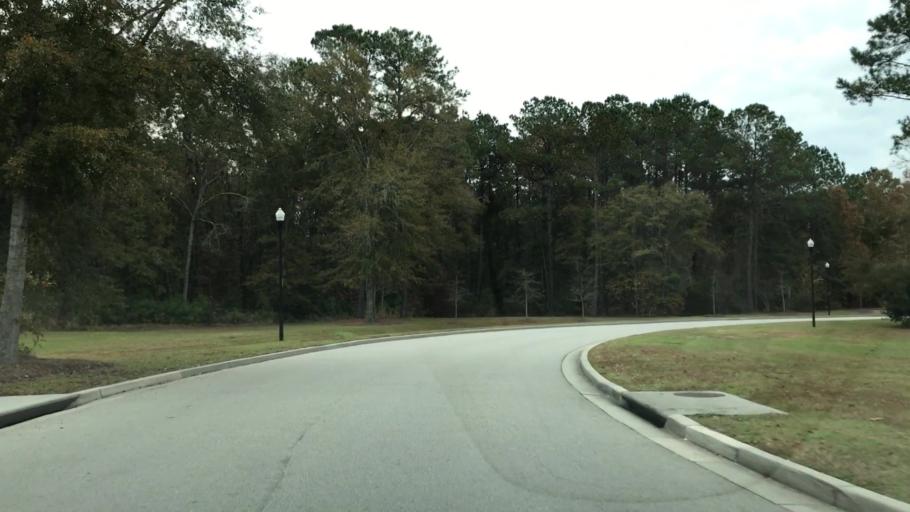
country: US
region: South Carolina
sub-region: Charleston County
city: Isle of Palms
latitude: 32.8880
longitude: -79.7453
